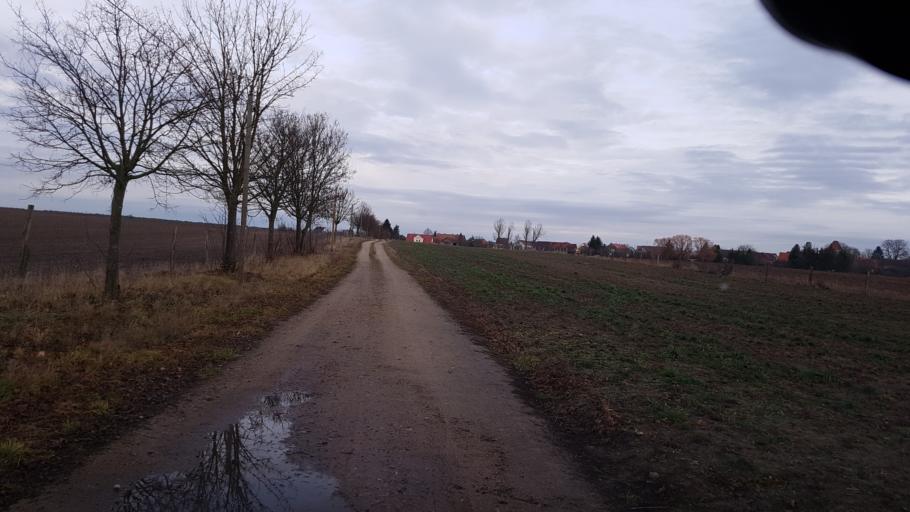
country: DE
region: Brandenburg
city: Hohenbucko
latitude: 51.7646
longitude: 13.4608
